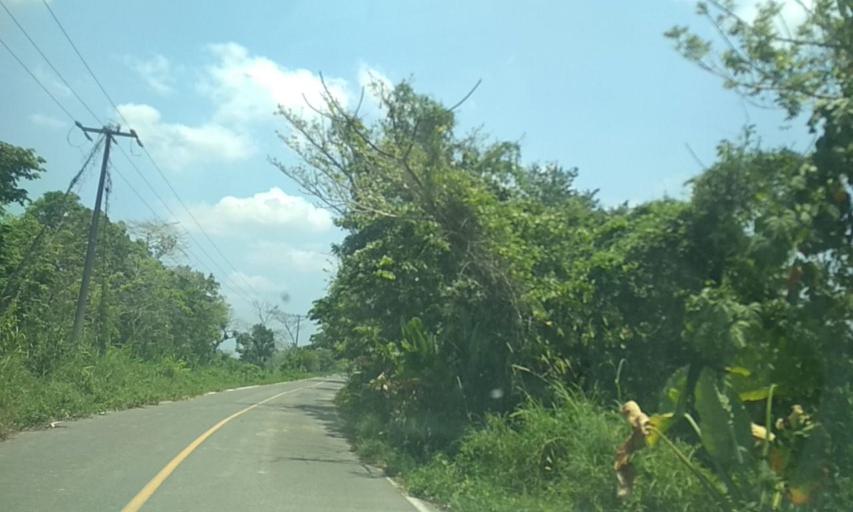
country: MX
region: Tabasco
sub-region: Huimanguillo
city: Francisco Rueda
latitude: 17.7608
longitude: -94.0219
